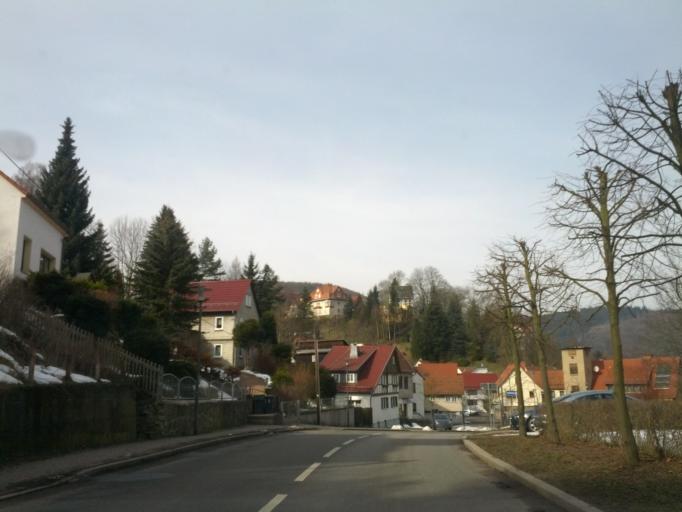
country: DE
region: Thuringia
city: Ruhla
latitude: 50.8875
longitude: 10.3700
